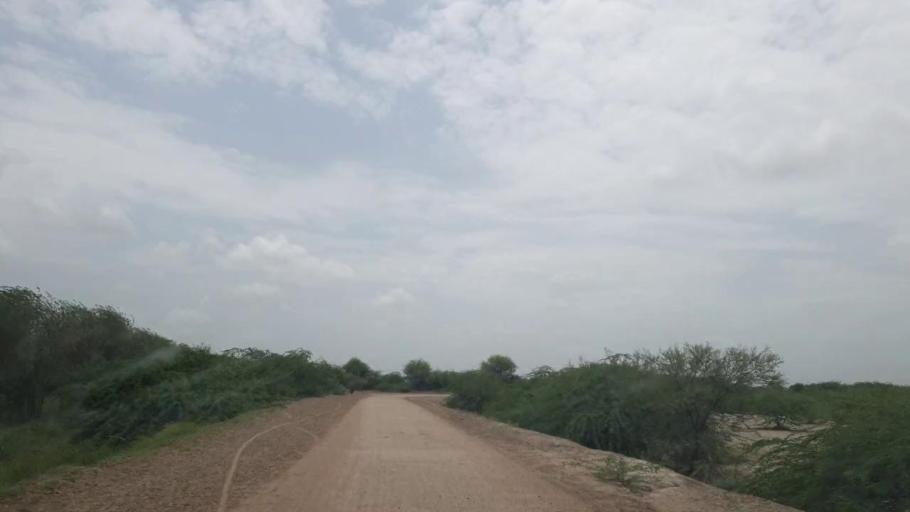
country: PK
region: Sindh
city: Naukot
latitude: 24.9315
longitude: 69.1797
